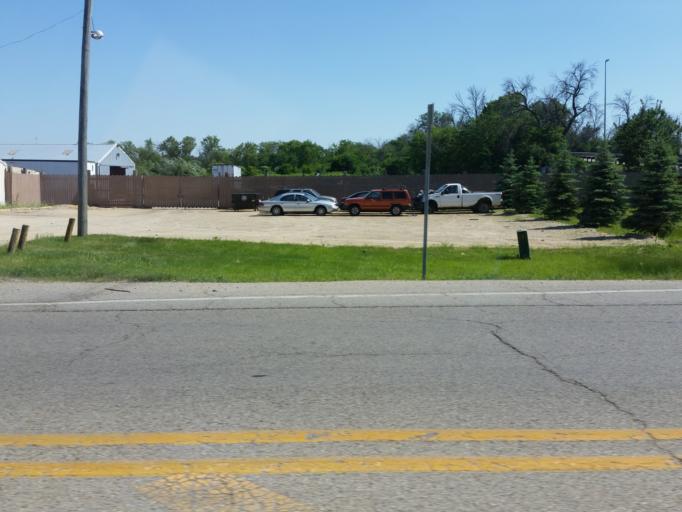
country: US
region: Illinois
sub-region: Ogle County
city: Davis Junction
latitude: 42.1017
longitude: -89.0756
